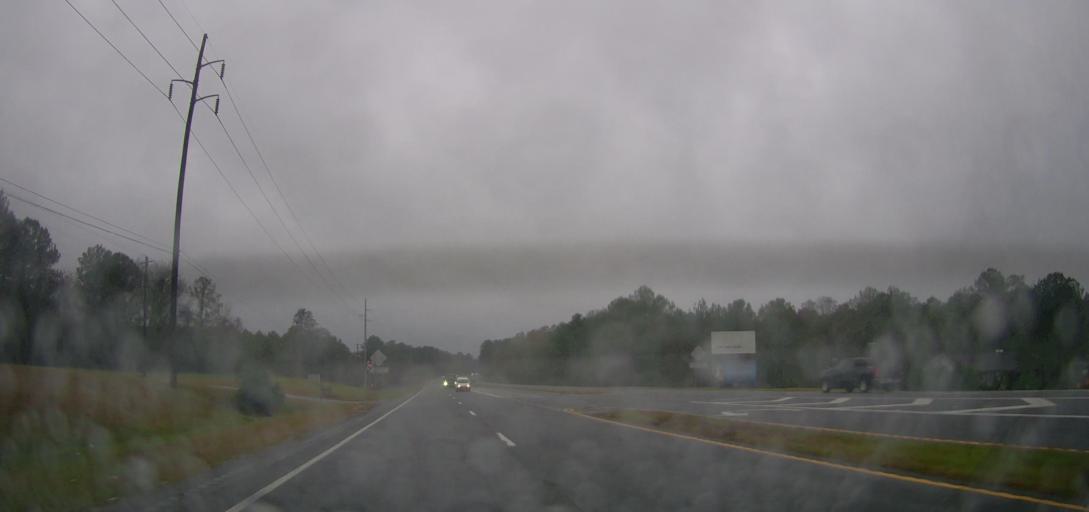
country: US
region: Georgia
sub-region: Jones County
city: Gray
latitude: 32.9382
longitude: -83.5804
